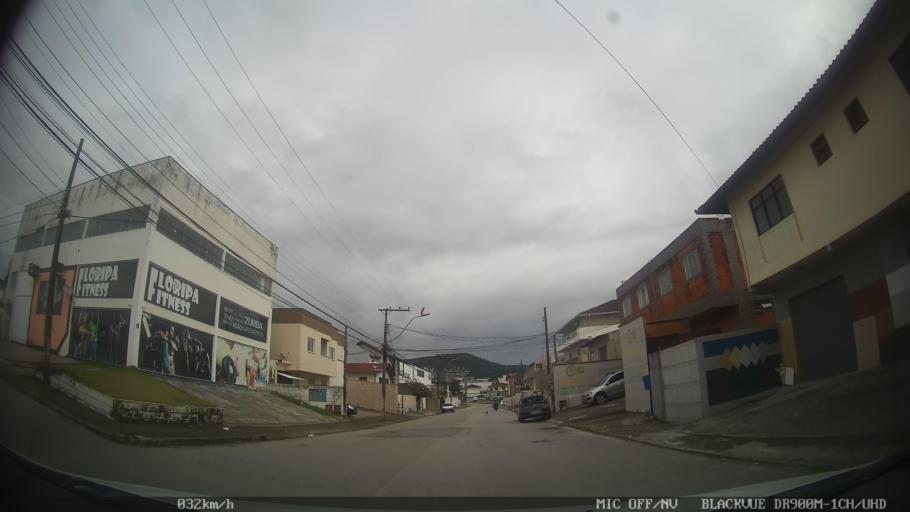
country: BR
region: Santa Catarina
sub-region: Sao Jose
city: Campinas
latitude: -27.5678
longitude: -48.6239
